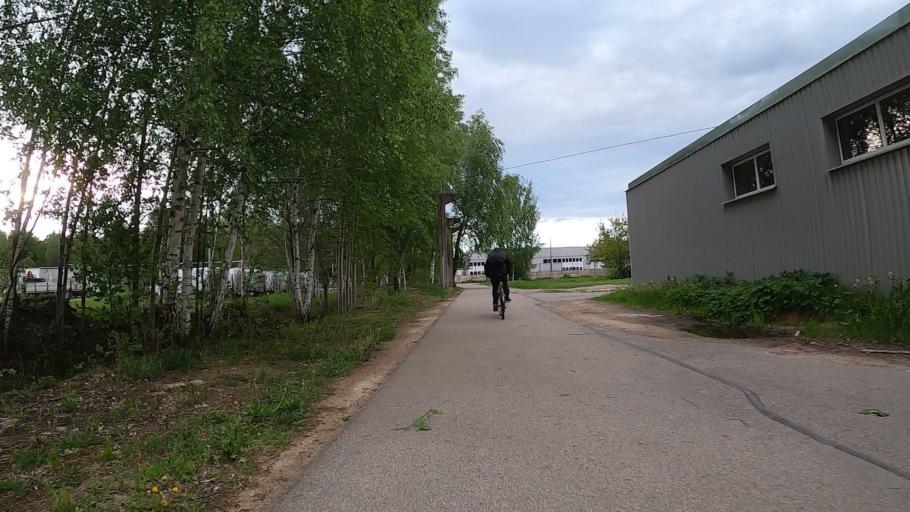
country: LV
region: Olaine
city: Olaine
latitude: 56.7937
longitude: 23.9268
